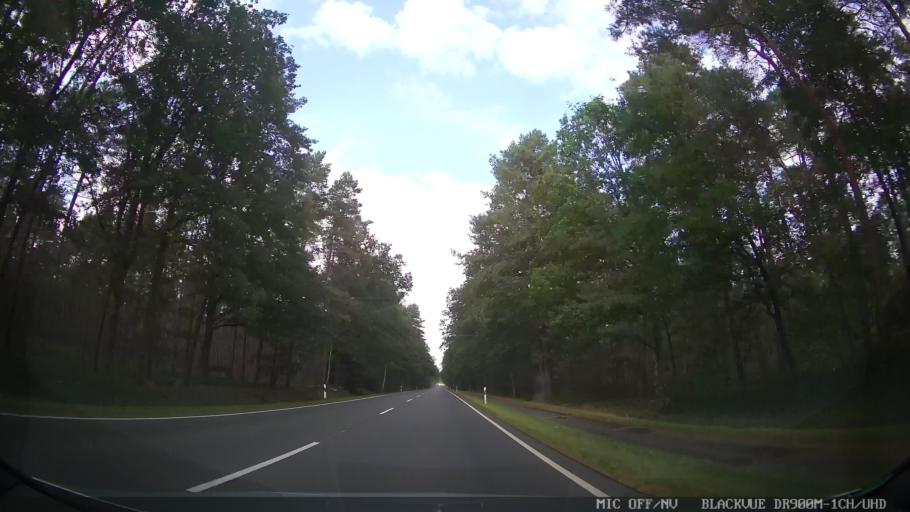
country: DE
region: Lower Saxony
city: Bergen
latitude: 52.7580
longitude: 9.9785
